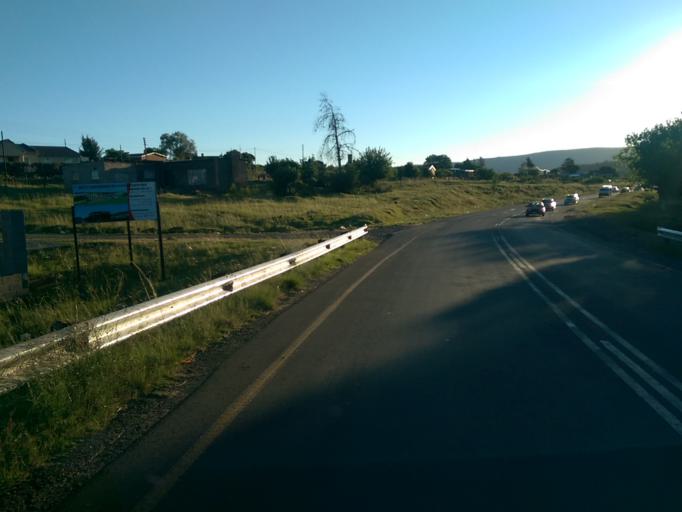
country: LS
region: Maseru
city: Maseru
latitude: -29.3875
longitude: 27.5598
